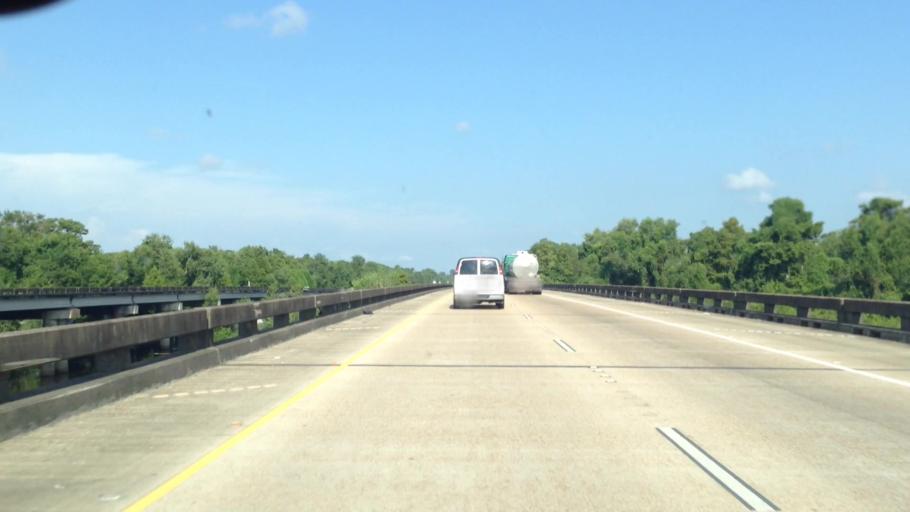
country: US
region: Louisiana
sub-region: Saint John the Baptist Parish
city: Reserve
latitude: 30.1114
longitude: -90.5457
